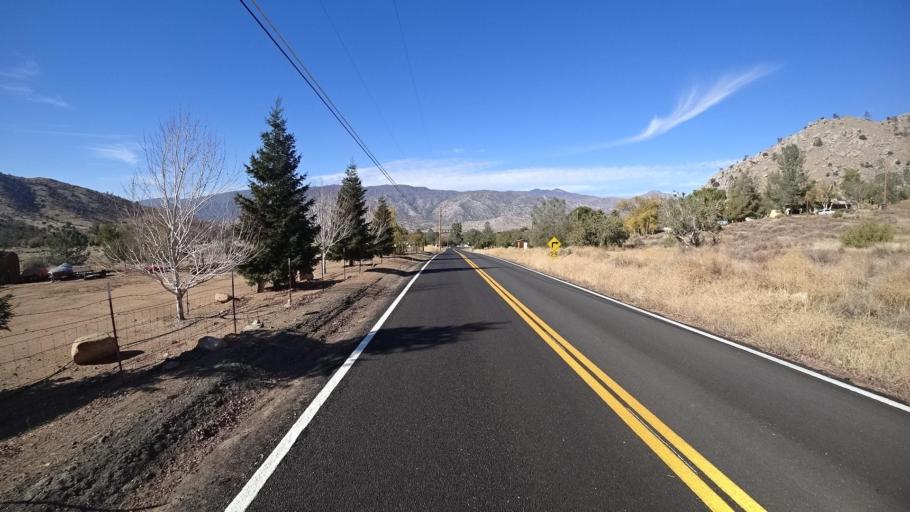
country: US
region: California
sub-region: Kern County
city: Lake Isabella
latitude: 35.6007
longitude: -118.4596
